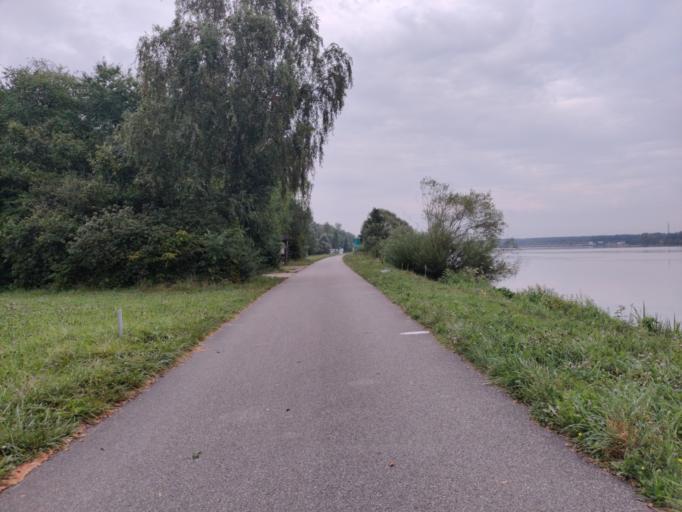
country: AT
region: Upper Austria
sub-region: Politischer Bezirk Linz-Land
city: Asten
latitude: 48.2561
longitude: 14.4191
